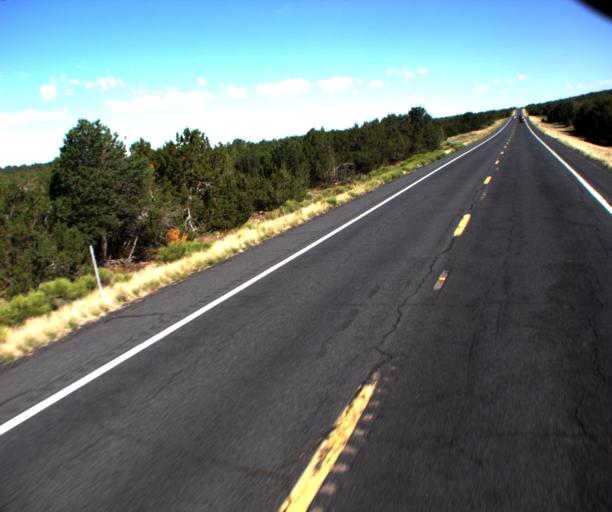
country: US
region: Arizona
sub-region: Coconino County
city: Williams
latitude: 35.3856
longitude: -112.1640
